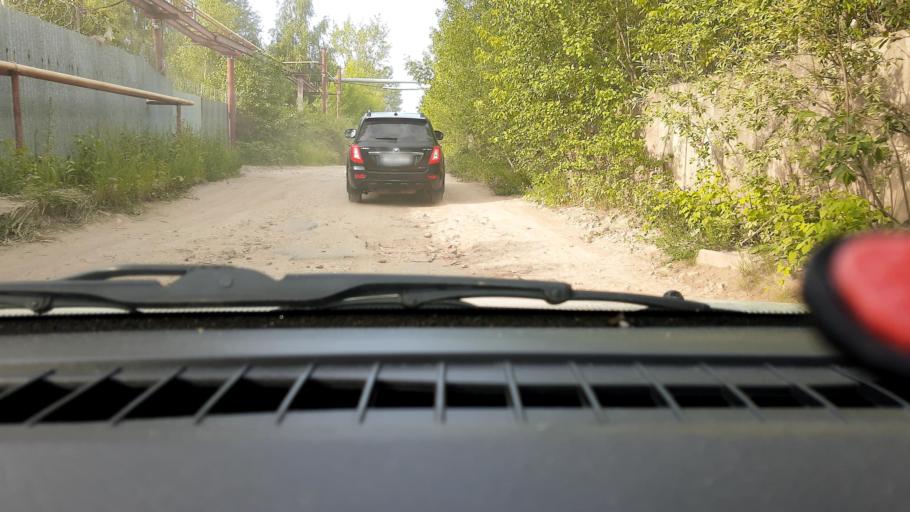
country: RU
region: Nizjnij Novgorod
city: Kstovo
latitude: 56.1236
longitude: 44.1374
